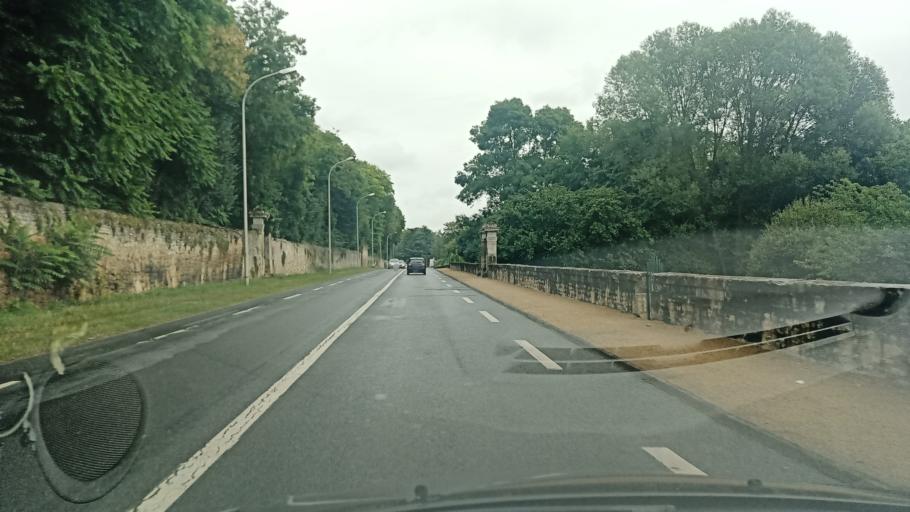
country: FR
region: Poitou-Charentes
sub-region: Departement de la Vienne
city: Poitiers
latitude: 46.6014
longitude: 0.3409
